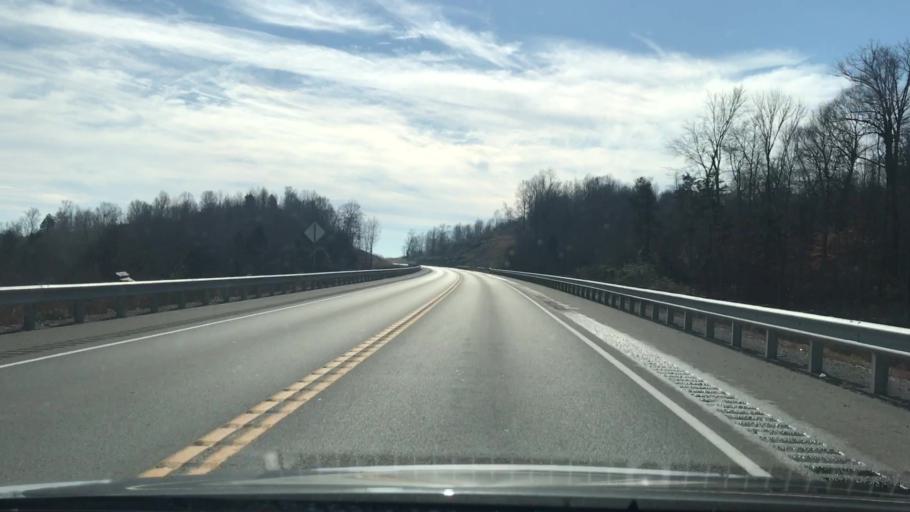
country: US
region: Kentucky
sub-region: Monroe County
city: Tompkinsville
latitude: 36.8250
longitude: -85.6879
